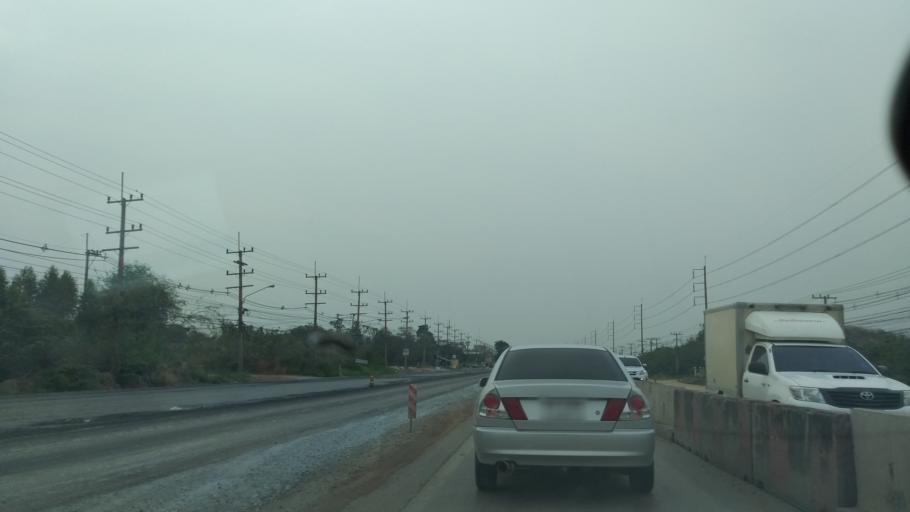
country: TH
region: Chachoengsao
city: Chachoengsao
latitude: 13.7547
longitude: 100.9977
